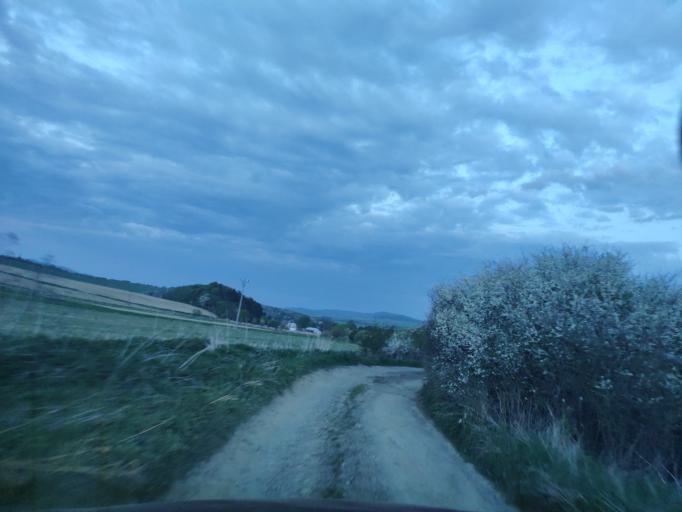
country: SK
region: Presovsky
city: Lipany
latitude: 49.1795
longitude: 20.8487
